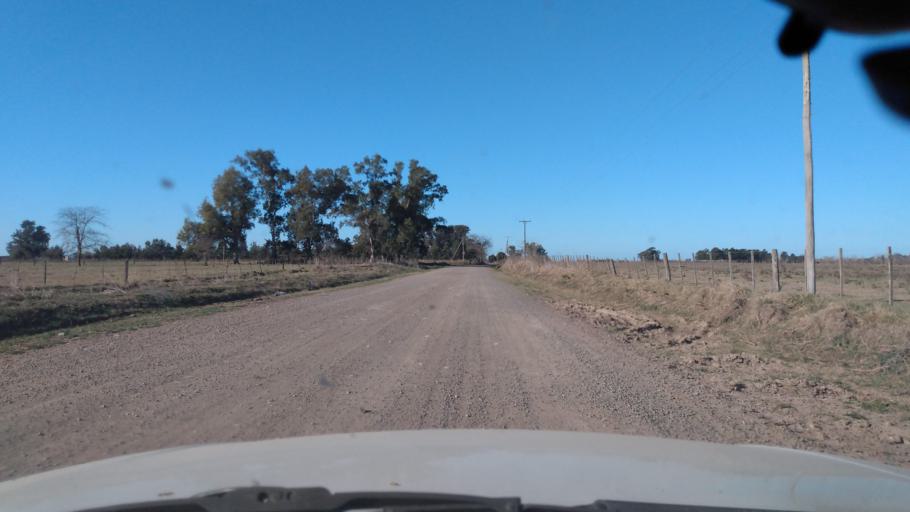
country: AR
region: Buenos Aires
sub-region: Partido de Mercedes
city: Mercedes
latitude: -34.6090
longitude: -59.3135
